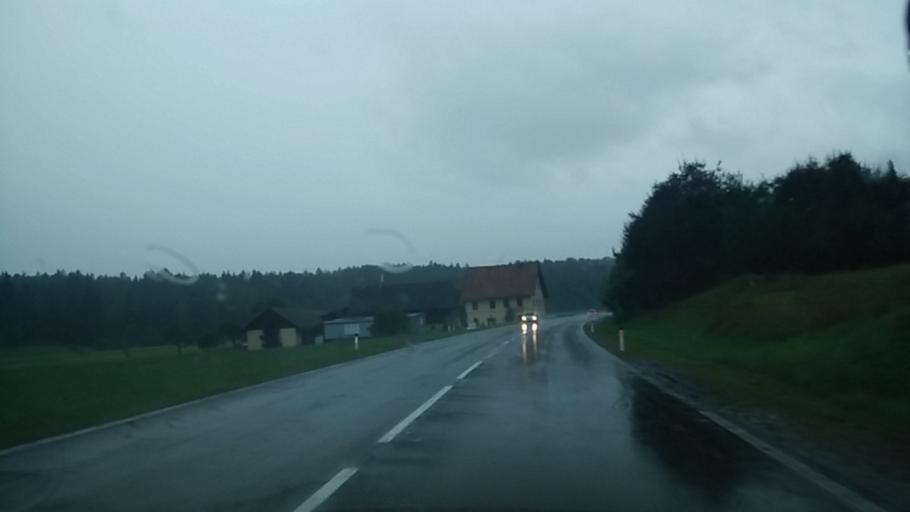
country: AT
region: Carinthia
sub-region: Politischer Bezirk Villach Land
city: Rosegg
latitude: 46.6075
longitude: 13.9866
